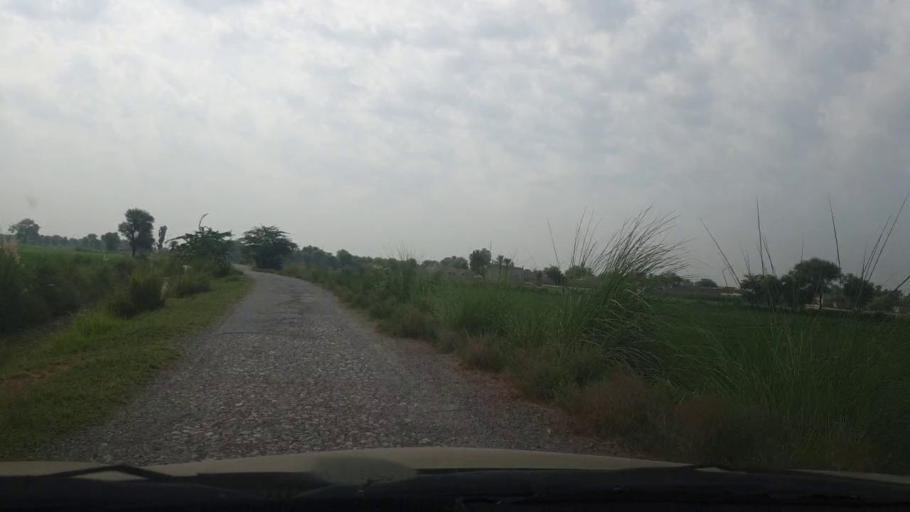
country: PK
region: Sindh
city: Larkana
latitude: 27.6402
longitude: 68.2039
